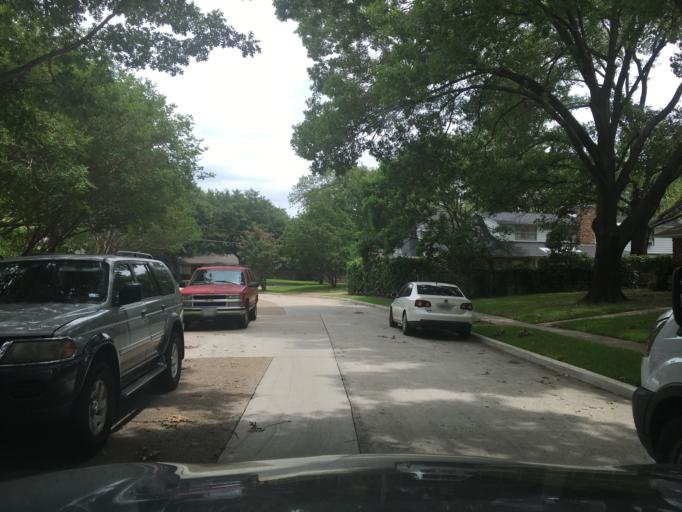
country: US
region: Texas
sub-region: Dallas County
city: Richardson
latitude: 32.9500
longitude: -96.7546
